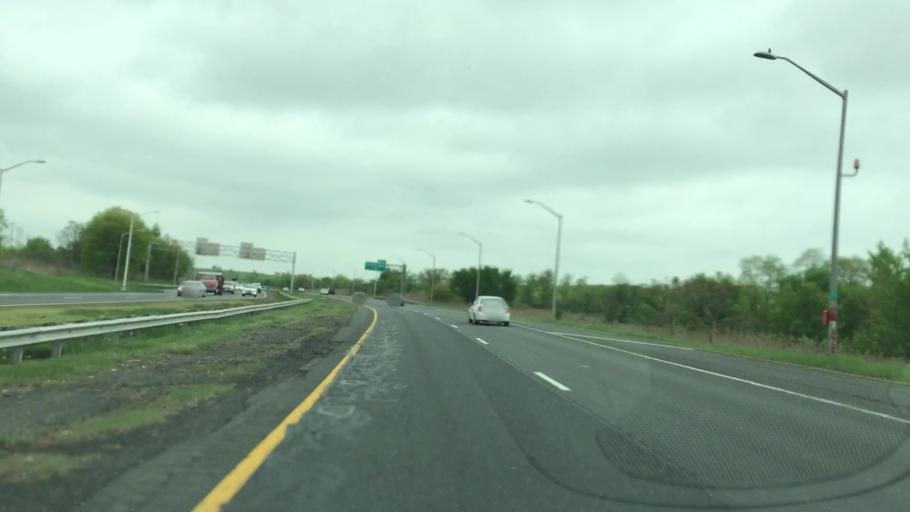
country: US
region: New Jersey
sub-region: Middlesex County
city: Carteret
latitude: 40.5695
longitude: -74.1908
